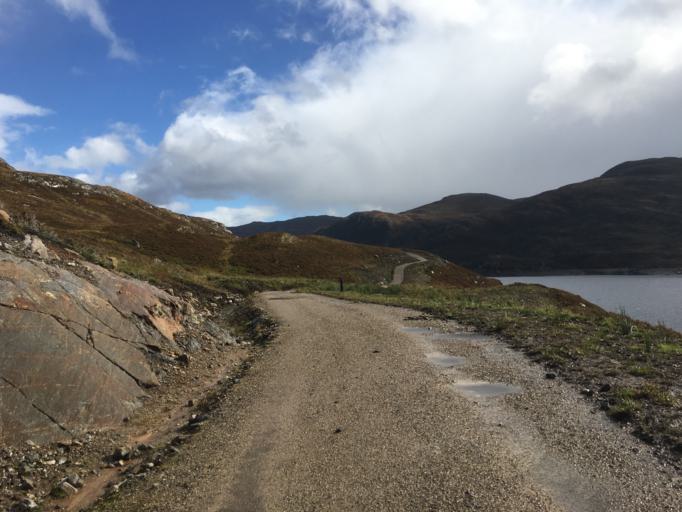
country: GB
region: Scotland
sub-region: Highland
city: Spean Bridge
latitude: 57.3410
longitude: -4.9747
